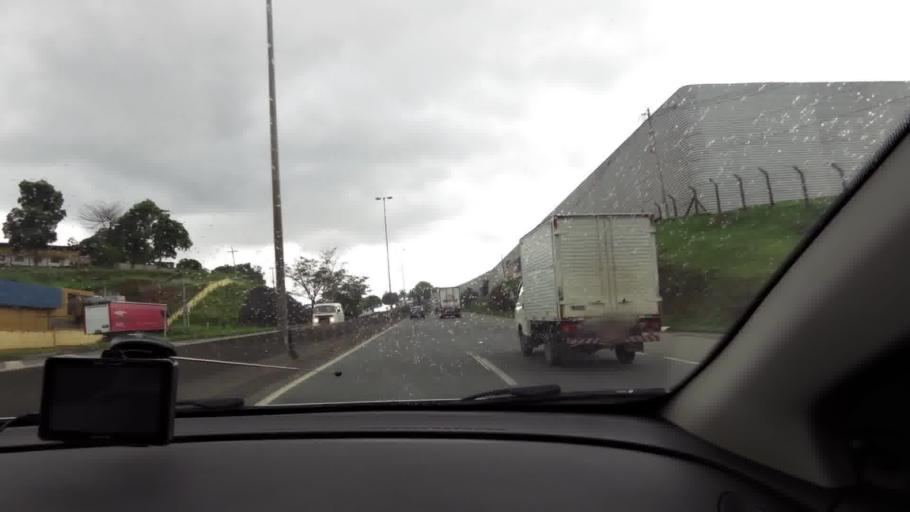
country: BR
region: Espirito Santo
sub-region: Viana
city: Viana
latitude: -20.3627
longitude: -40.4380
